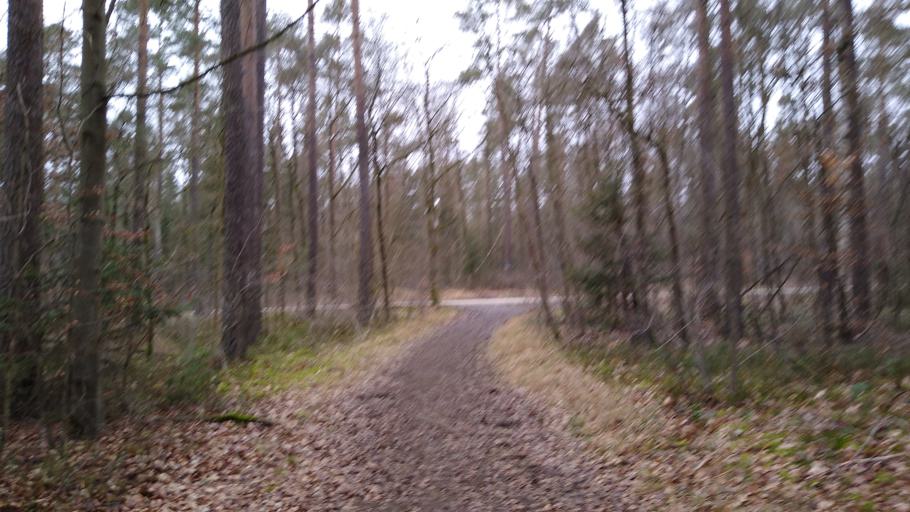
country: DE
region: Bavaria
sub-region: Regierungsbezirk Mittelfranken
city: Heroldsberg
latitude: 49.4885
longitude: 11.1345
